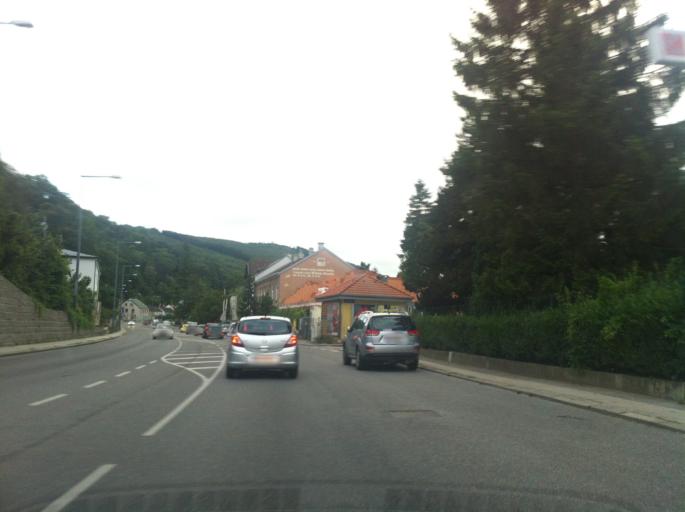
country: AT
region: Lower Austria
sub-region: Politischer Bezirk Wien-Umgebung
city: Purkersdorf
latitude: 48.2080
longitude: 16.2092
